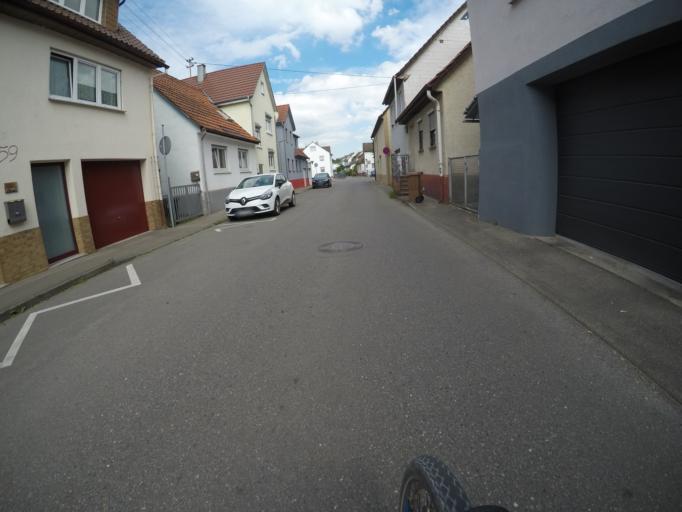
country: DE
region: Baden-Wuerttemberg
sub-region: Regierungsbezirk Stuttgart
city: Wendlingen am Neckar
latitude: 48.6781
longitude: 9.3820
